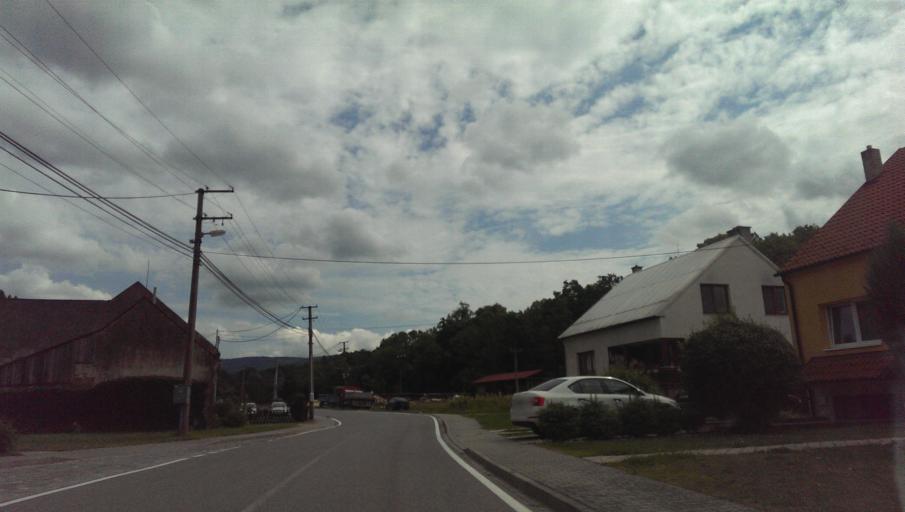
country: CZ
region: South Moravian
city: Velka nad Velickou
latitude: 48.8841
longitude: 17.5788
